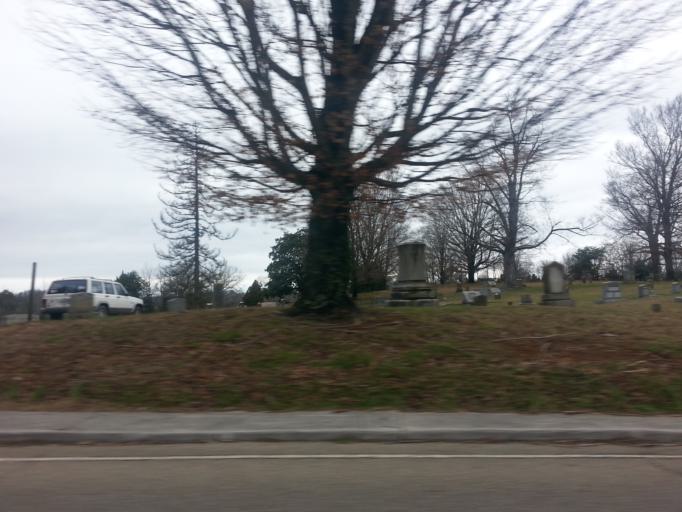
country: US
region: Tennessee
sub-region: Jefferson County
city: Jefferson City
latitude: 36.1209
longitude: -83.5031
